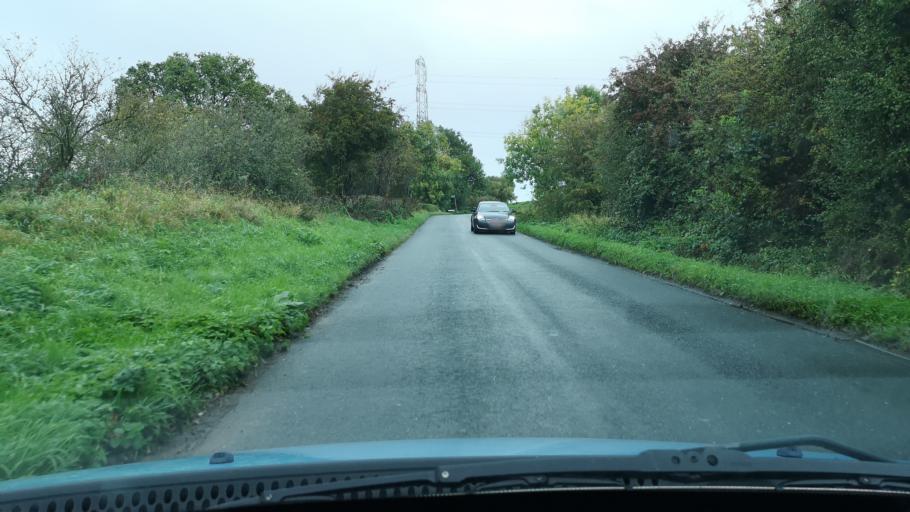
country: GB
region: England
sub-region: Doncaster
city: Hatfield
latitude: 53.6244
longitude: -0.9830
